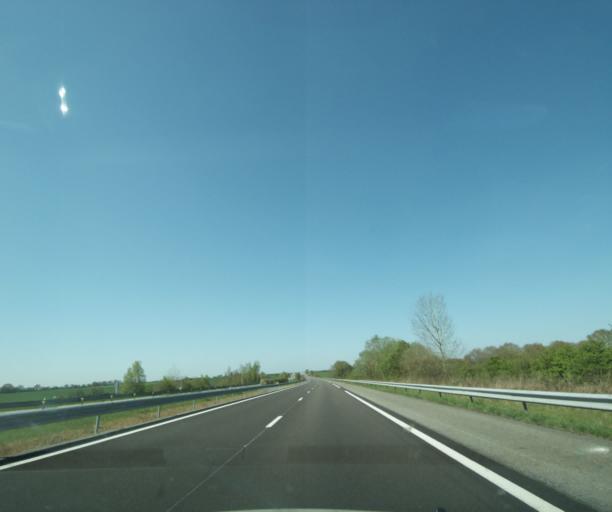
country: FR
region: Bourgogne
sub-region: Departement de la Nievre
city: Neuvy-sur-Loire
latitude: 47.5164
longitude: 2.9164
